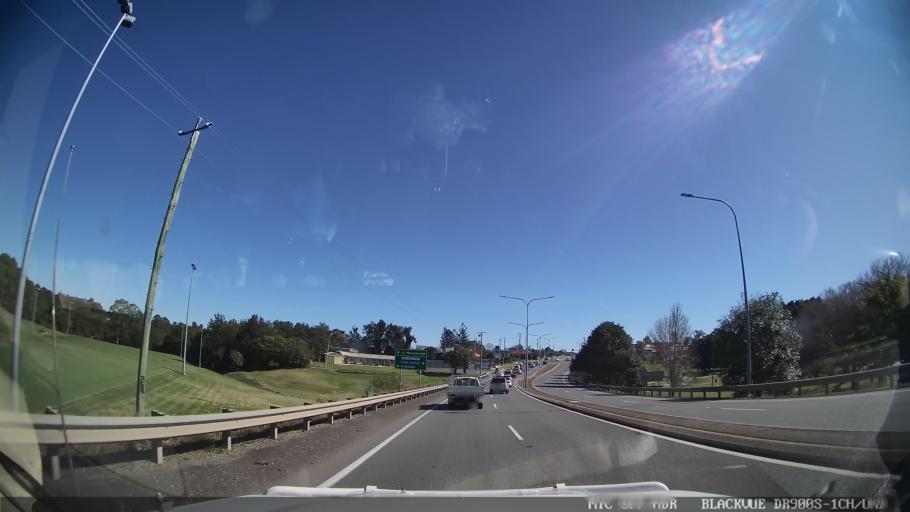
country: AU
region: Queensland
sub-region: Gympie Regional Council
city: Gympie
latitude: -26.1935
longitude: 152.6598
